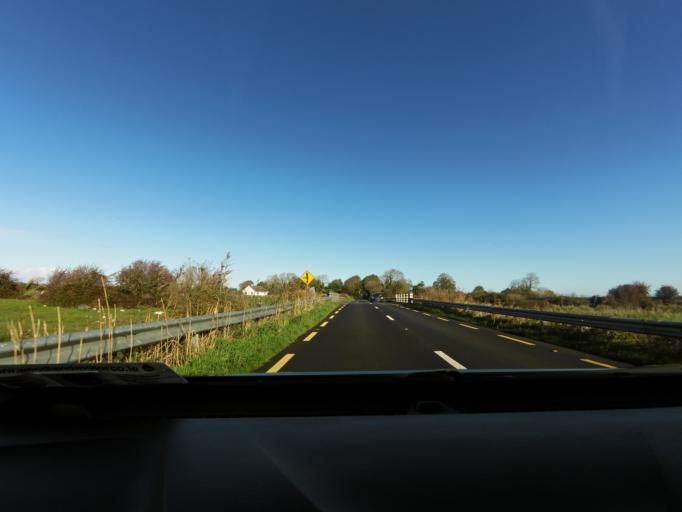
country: IE
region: Connaught
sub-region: County Galway
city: Claregalway
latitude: 53.3605
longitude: -9.0176
